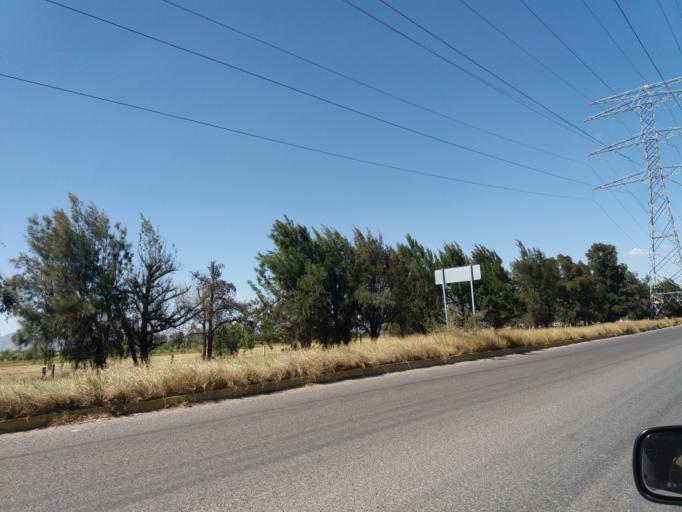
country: MX
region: Aguascalientes
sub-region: Aguascalientes
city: San Sebastian [Fraccionamiento]
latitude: 21.8195
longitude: -102.2938
